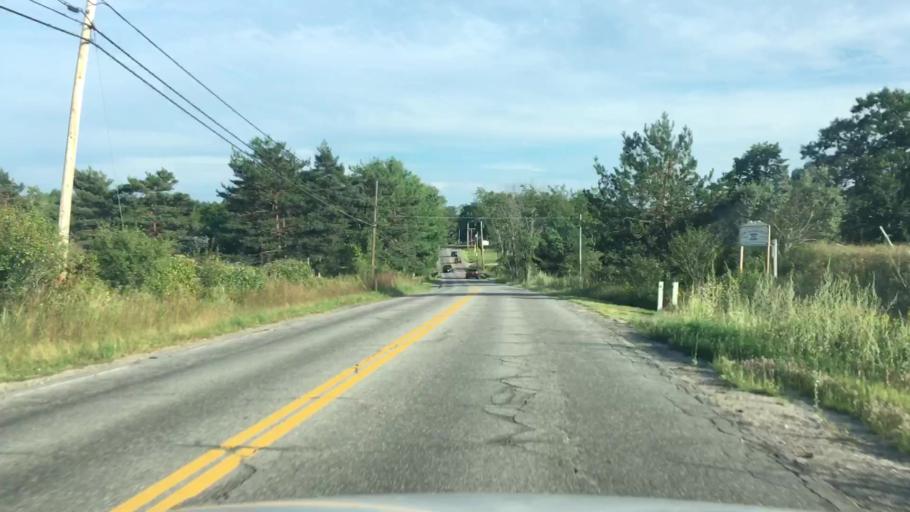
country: US
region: Maine
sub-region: Cumberland County
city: South Windham
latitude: 43.7276
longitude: -70.4075
